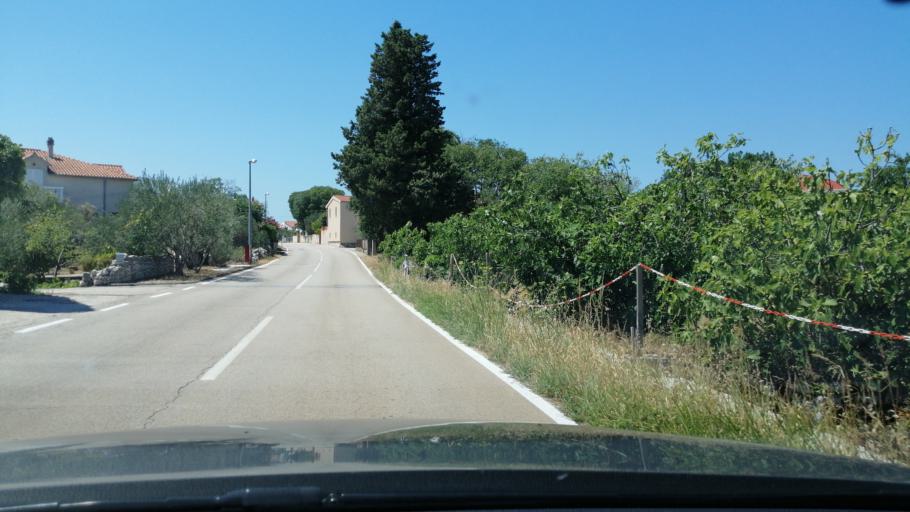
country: HR
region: Sibensko-Kniniska
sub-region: Grad Sibenik
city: Pirovac
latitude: 43.8219
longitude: 15.6732
